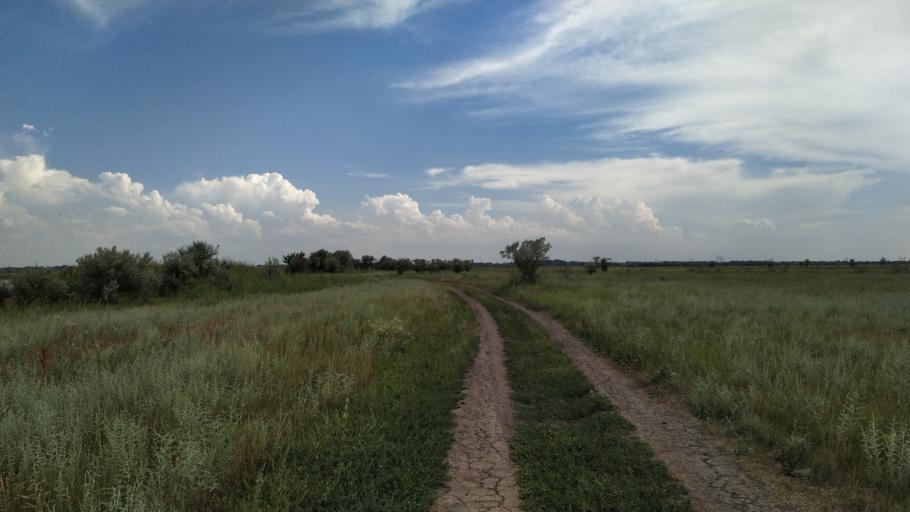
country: RU
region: Rostov
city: Kuleshovka
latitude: 47.1330
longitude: 39.6300
